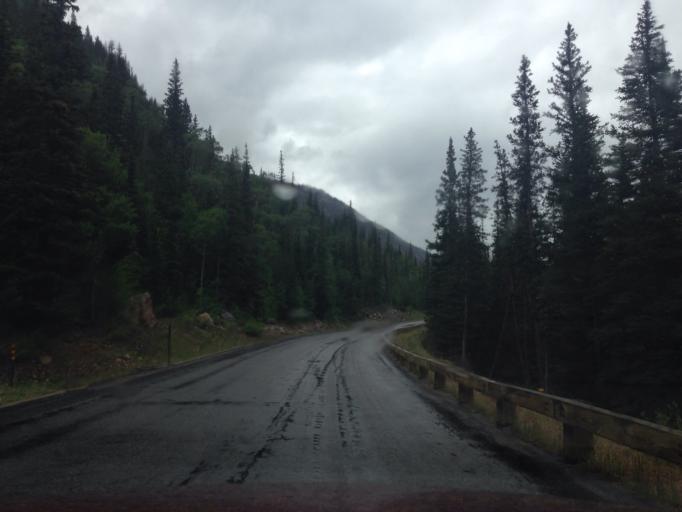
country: US
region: Colorado
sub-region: Clear Creek County
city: Georgetown
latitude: 39.6408
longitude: -105.7076
